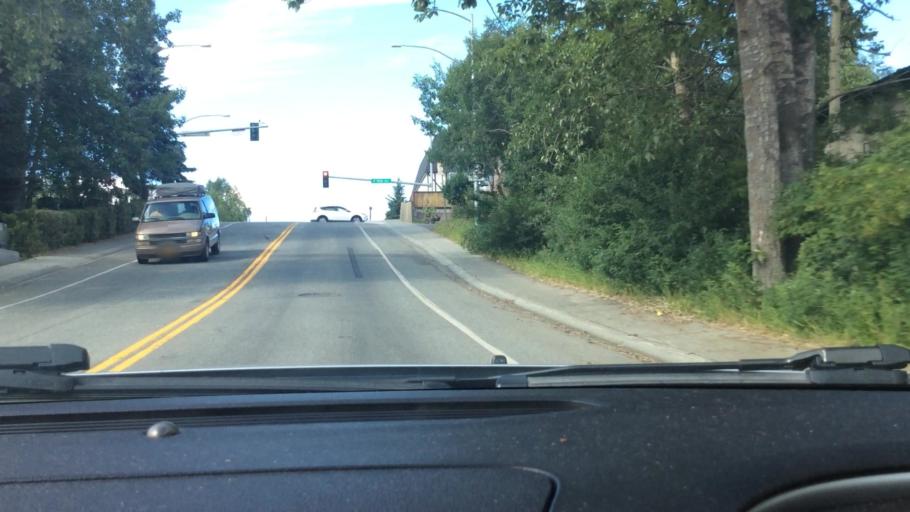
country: US
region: Alaska
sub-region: Anchorage Municipality
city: Anchorage
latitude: 61.2070
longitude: -149.8792
